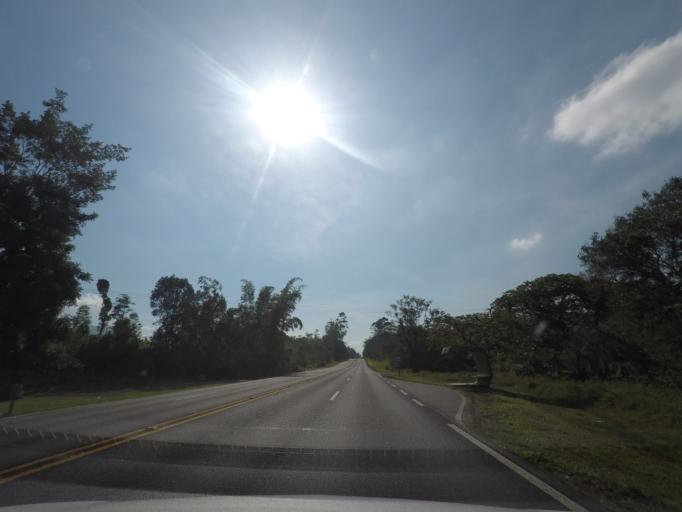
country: BR
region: Parana
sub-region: Pontal Do Parana
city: Pontal do Parana
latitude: -25.6110
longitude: -48.6048
